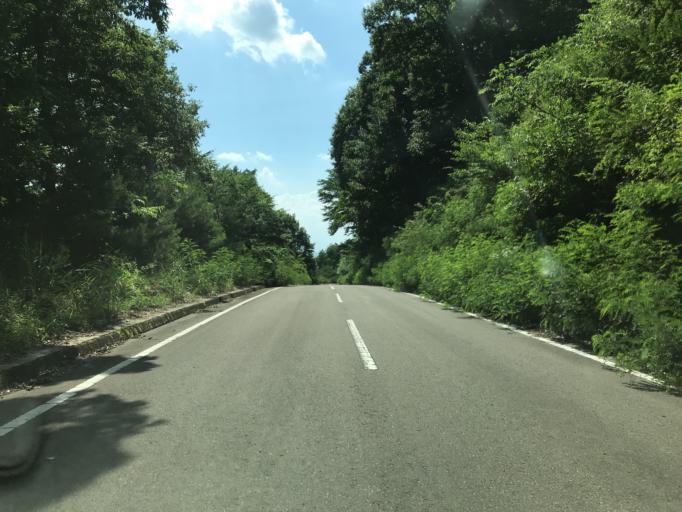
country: JP
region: Fukushima
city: Yanagawamachi-saiwaicho
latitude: 37.7664
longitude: 140.6758
